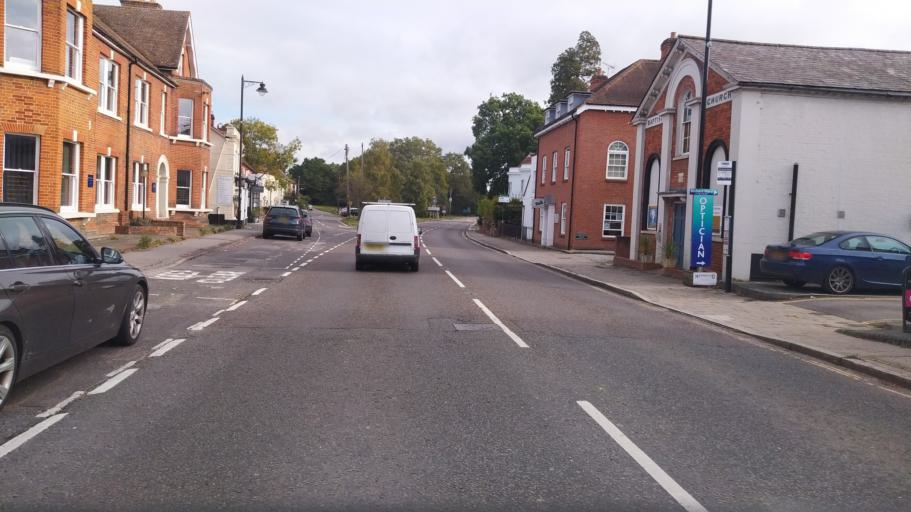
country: GB
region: England
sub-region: Hampshire
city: Eversley
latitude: 51.3072
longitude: -0.8985
